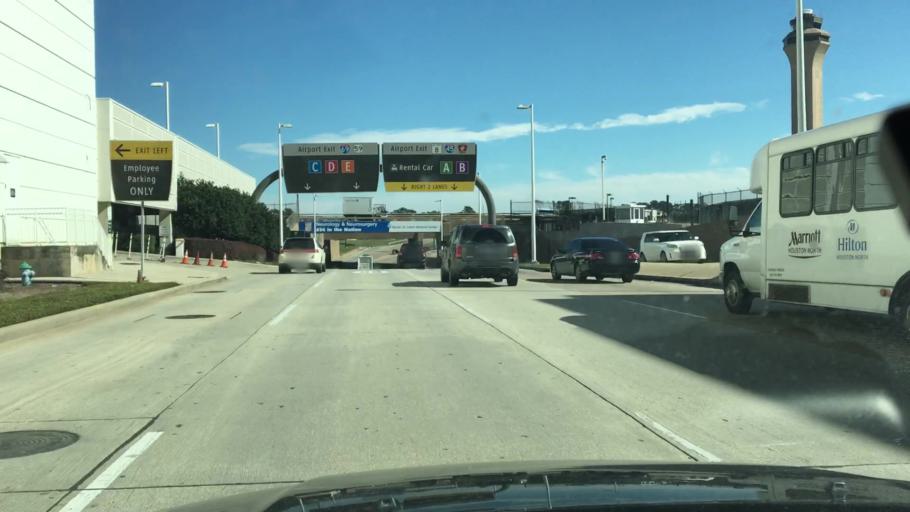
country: US
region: Texas
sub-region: Harris County
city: Humble
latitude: 29.9859
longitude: -95.3322
